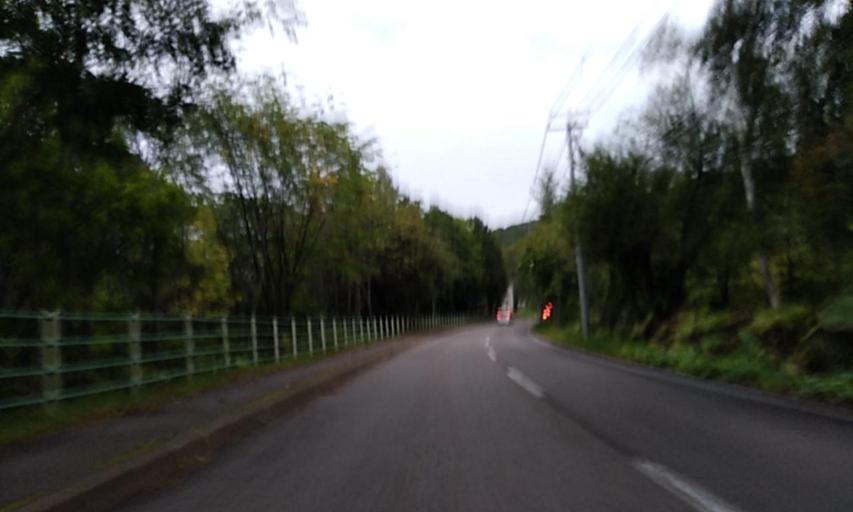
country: JP
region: Hokkaido
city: Abashiri
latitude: 44.0005
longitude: 144.2294
